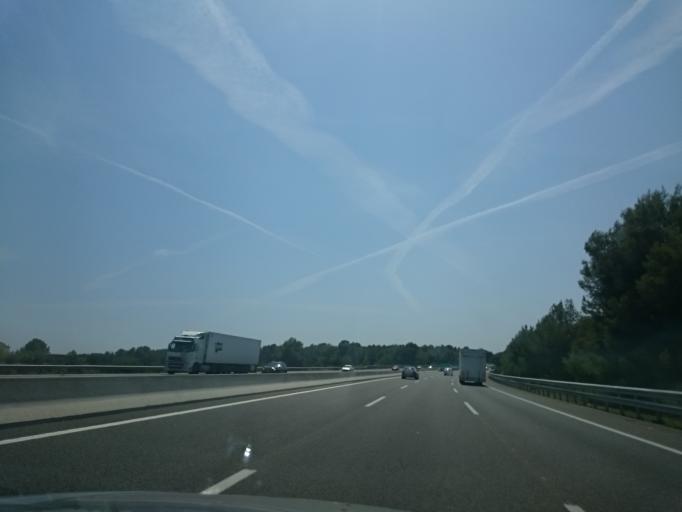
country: ES
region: Catalonia
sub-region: Provincia de Tarragona
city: Sant Jaume dels Domenys
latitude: 41.2934
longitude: 1.5981
